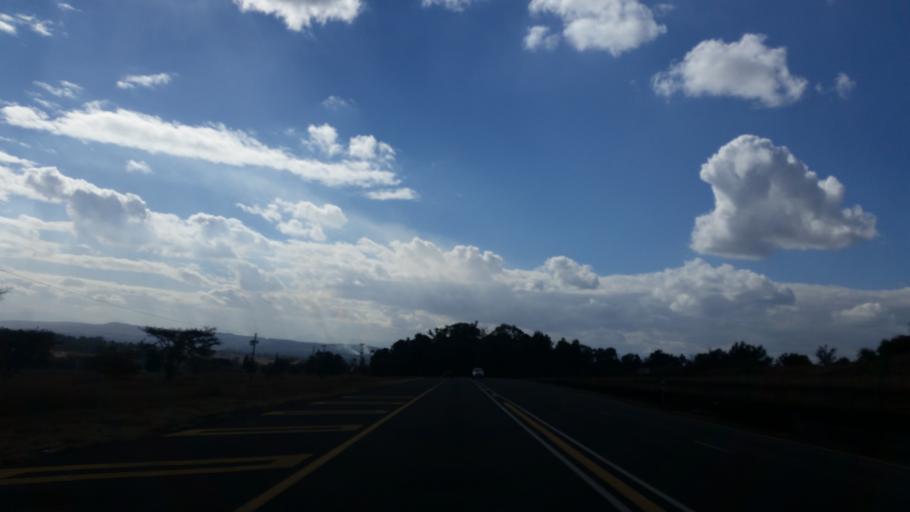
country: ZA
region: KwaZulu-Natal
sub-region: Amajuba District Municipality
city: Newcastle
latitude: -27.8028
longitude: 29.9562
